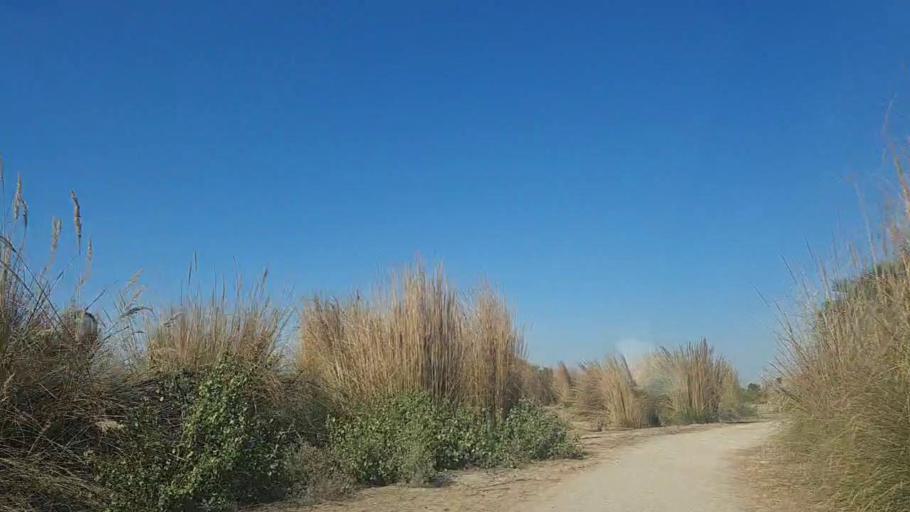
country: PK
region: Sindh
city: Khadro
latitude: 26.2182
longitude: 68.8591
